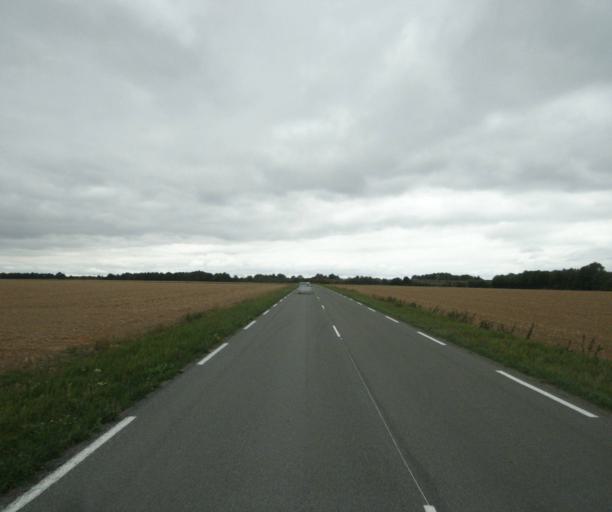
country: FR
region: Nord-Pas-de-Calais
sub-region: Departement du Nord
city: Fretin
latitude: 50.5662
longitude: 3.1580
